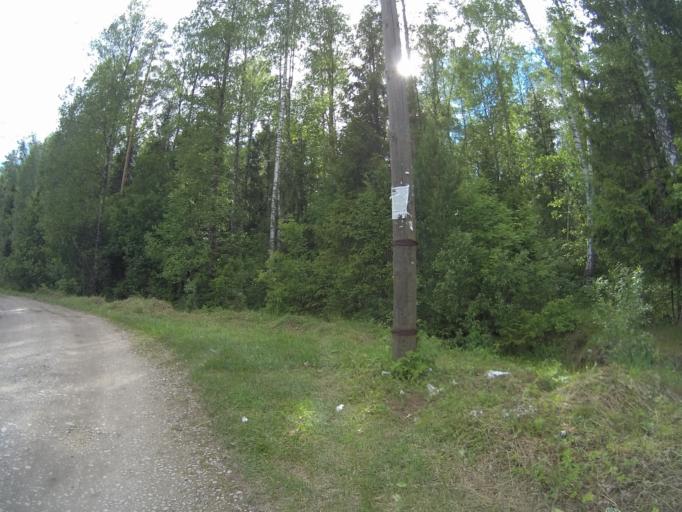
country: RU
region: Vladimir
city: Bogolyubovo
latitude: 56.1049
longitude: 40.5505
